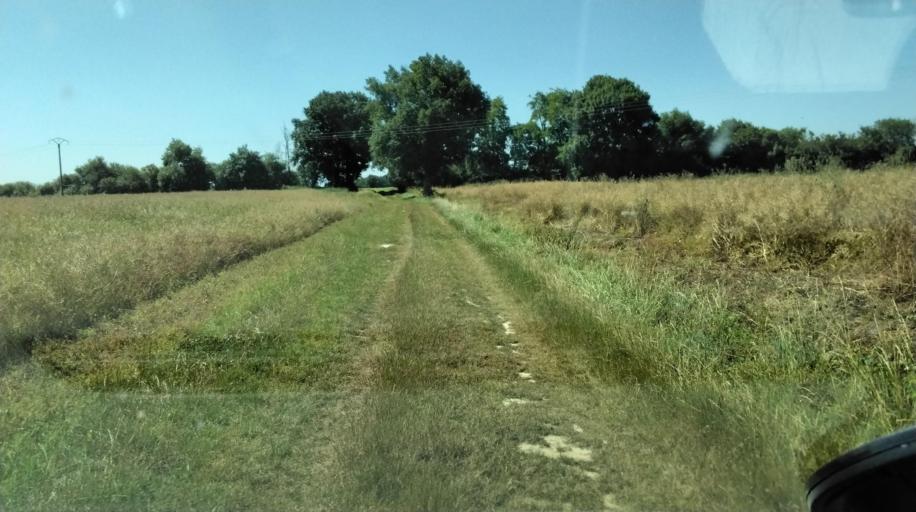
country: FR
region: Midi-Pyrenees
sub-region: Departement de la Haute-Garonne
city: Sainte-Foy-de-Peyrolieres
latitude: 43.4906
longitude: 1.1564
